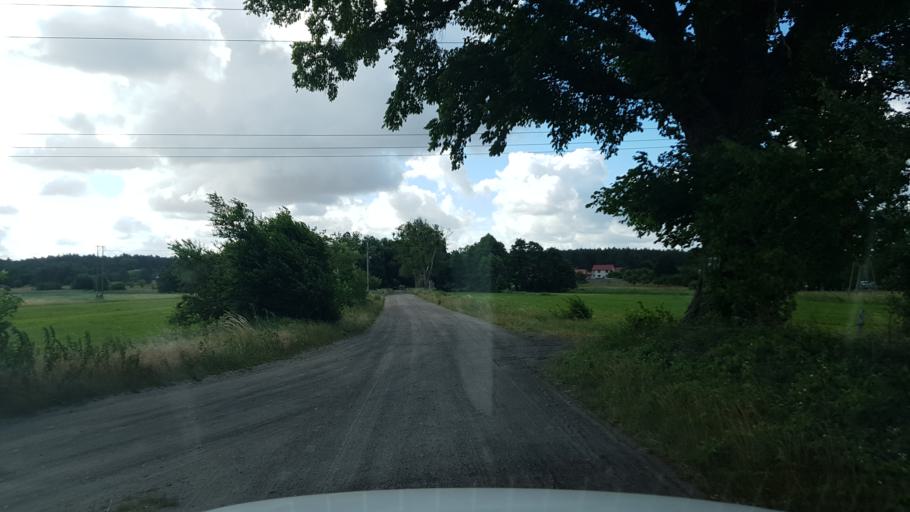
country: PL
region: West Pomeranian Voivodeship
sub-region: Powiat mysliborski
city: Debno
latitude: 52.7159
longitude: 14.6547
